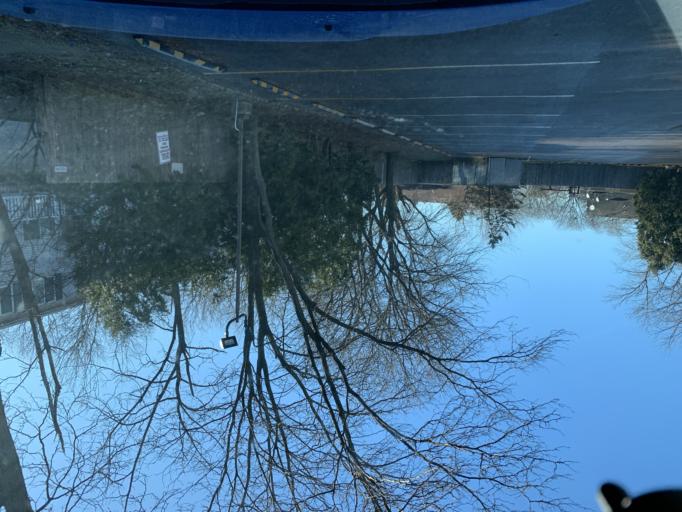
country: US
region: Wisconsin
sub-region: Dane County
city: Middleton
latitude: 43.0433
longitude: -89.5031
